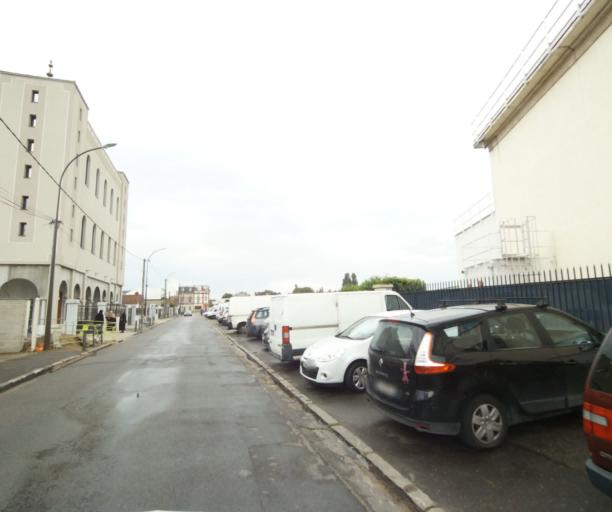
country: FR
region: Ile-de-France
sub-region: Departement du Val-d'Oise
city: Bezons
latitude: 48.9339
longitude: 2.2302
